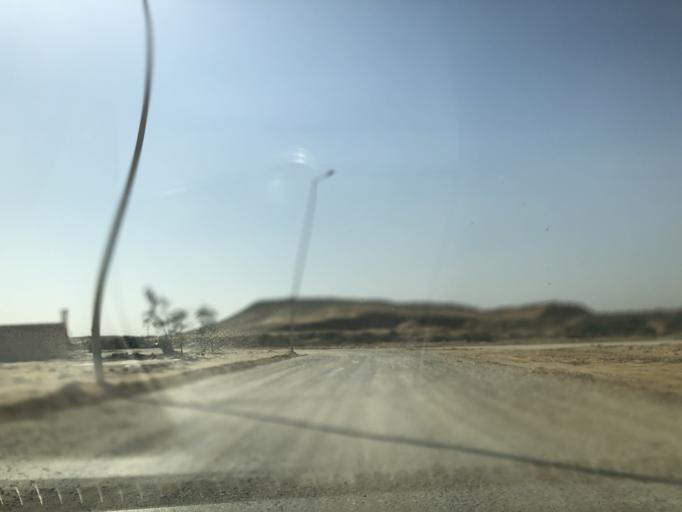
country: EG
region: Al Jizah
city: Madinat Sittah Uktubar
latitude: 29.9335
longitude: 30.9565
